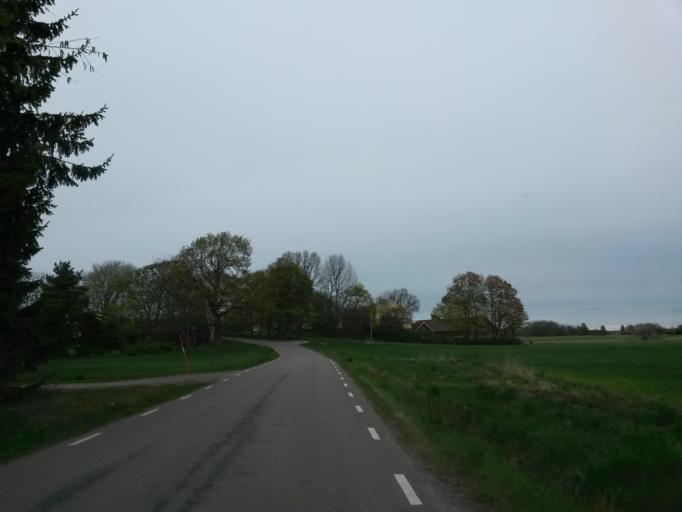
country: SE
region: Vaestra Goetaland
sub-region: Grastorps Kommun
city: Graestorp
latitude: 58.3354
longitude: 12.7636
